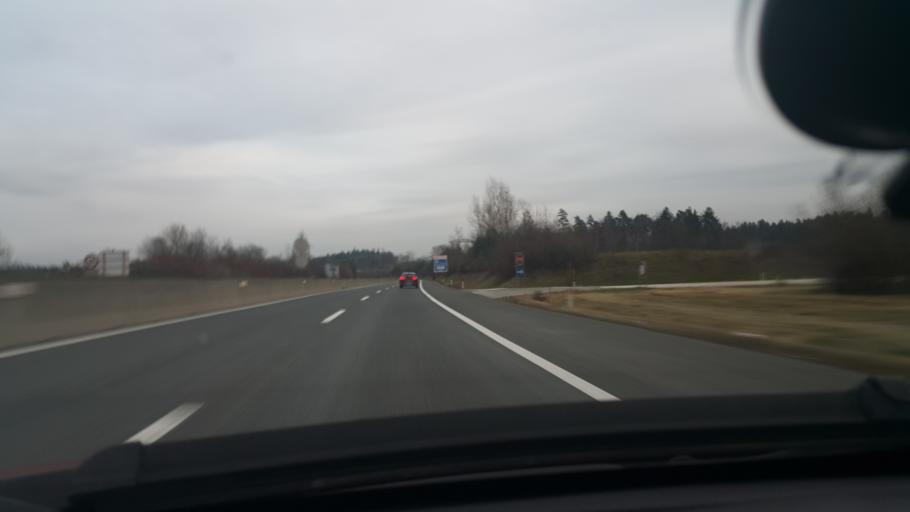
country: AT
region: Carinthia
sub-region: Politischer Bezirk Klagenfurt Land
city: Ebenthal
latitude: 46.6459
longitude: 14.3905
